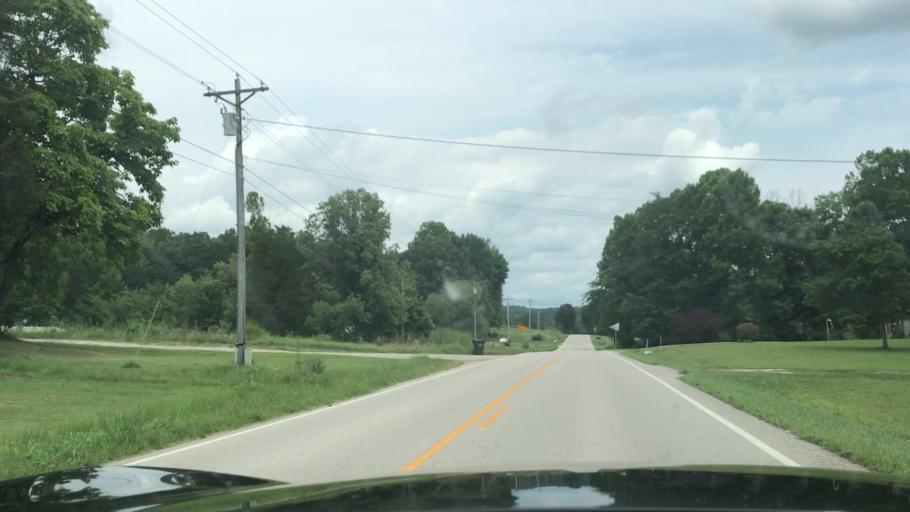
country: US
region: Kentucky
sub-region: Butler County
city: Morgantown
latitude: 37.1901
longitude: -86.7528
